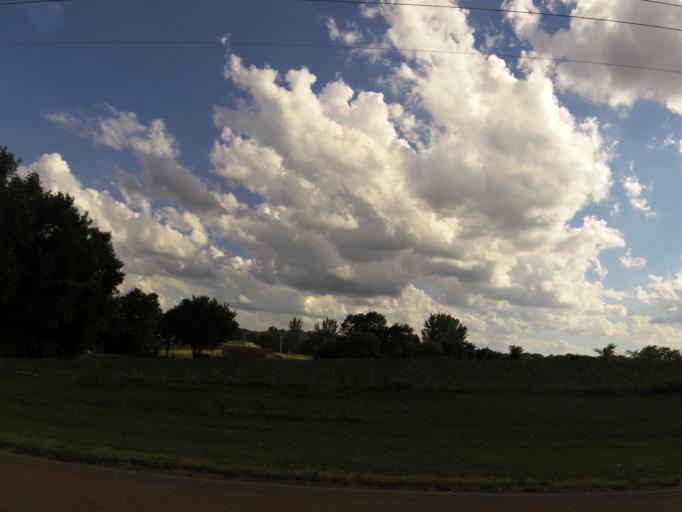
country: US
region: Minnesota
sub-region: Carver County
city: Waconia
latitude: 44.8198
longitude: -93.7337
